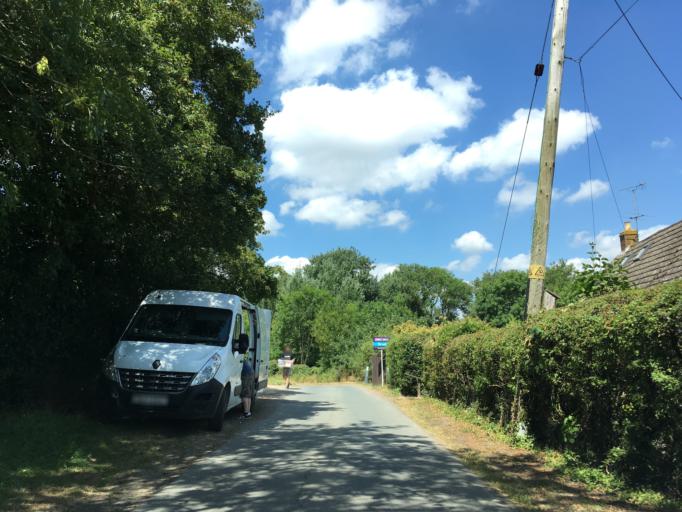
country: GB
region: England
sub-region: Gloucestershire
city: Shurdington
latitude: 51.8487
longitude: -2.1212
